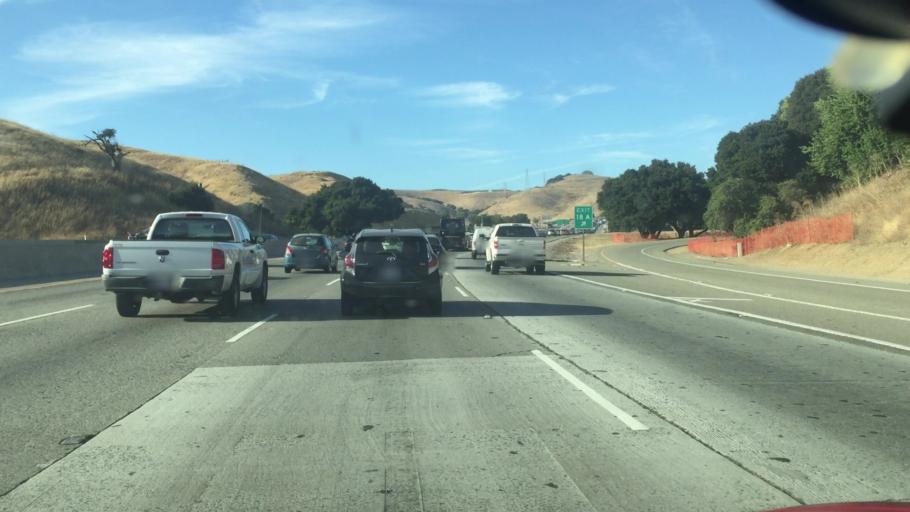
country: US
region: California
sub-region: Alameda County
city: Fremont
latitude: 37.5481
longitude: -121.9196
